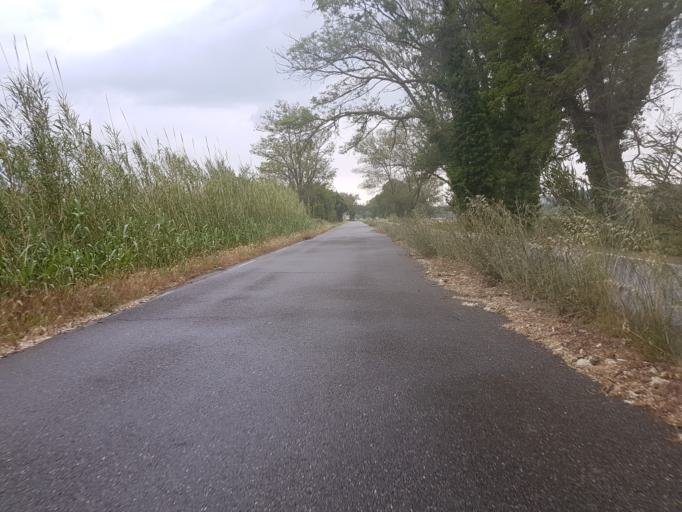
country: FR
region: Provence-Alpes-Cote d'Azur
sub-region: Departement du Vaucluse
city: Avignon
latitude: 43.9607
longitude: 4.8121
